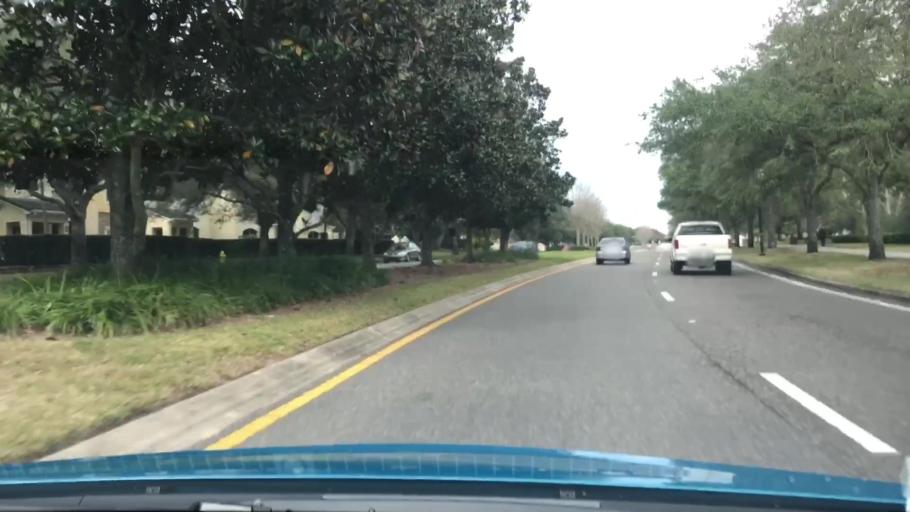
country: US
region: Florida
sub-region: Seminole County
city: Heathrow
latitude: 28.7821
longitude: -81.3580
